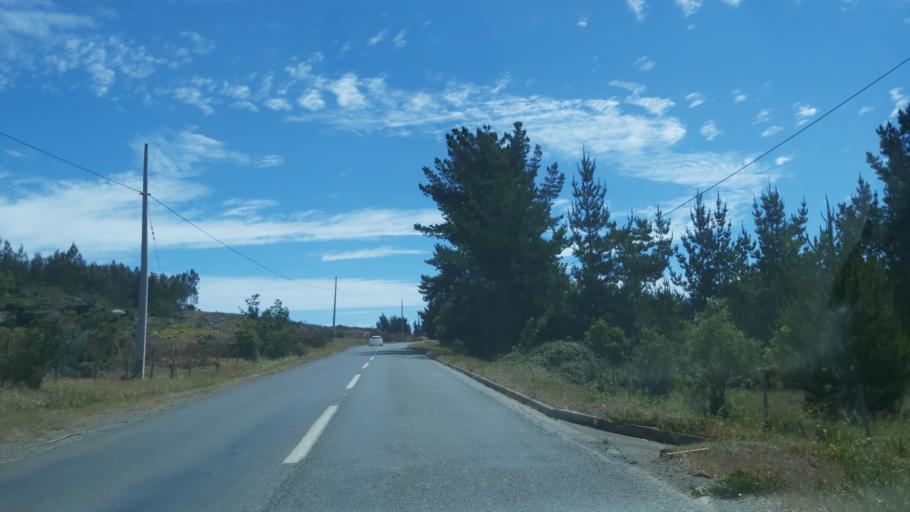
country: CL
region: Maule
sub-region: Provincia de Talca
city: Constitucion
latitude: -35.5390
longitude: -72.5522
